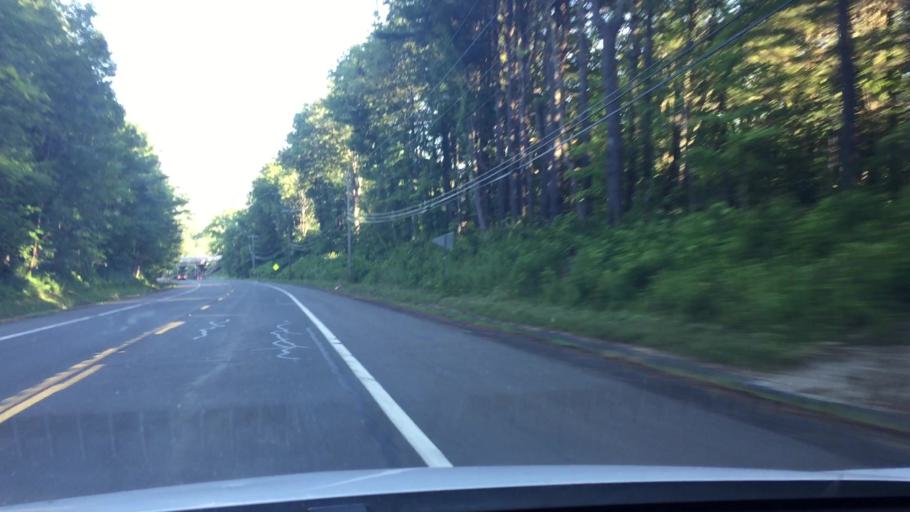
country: US
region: Massachusetts
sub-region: Berkshire County
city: Otis
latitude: 42.2596
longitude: -73.1236
